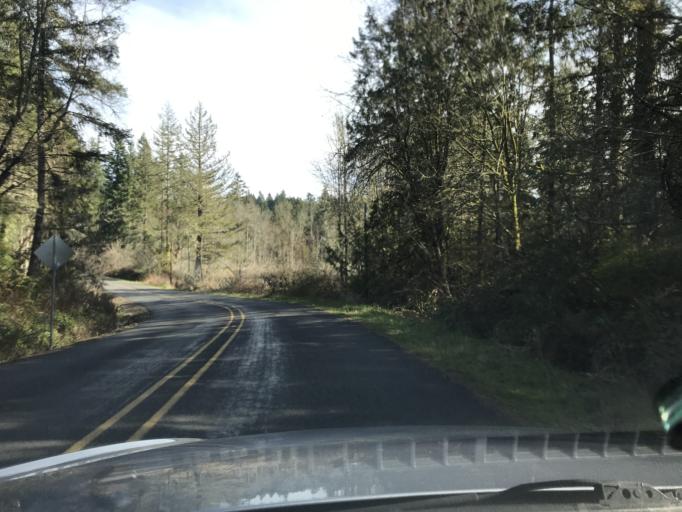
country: US
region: Washington
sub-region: Pierce County
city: Home
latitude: 47.2507
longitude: -122.7567
